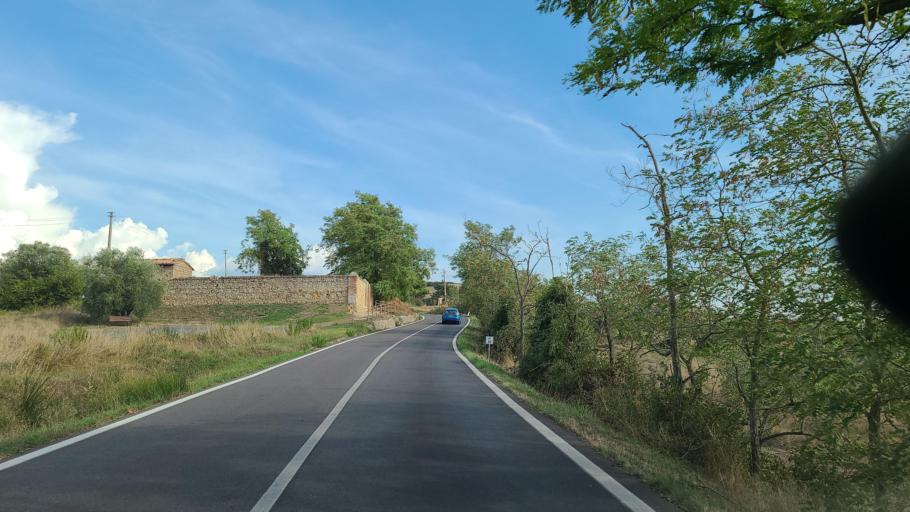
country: IT
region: Tuscany
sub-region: Province of Pisa
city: Volterra
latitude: 43.3913
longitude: 10.8979
